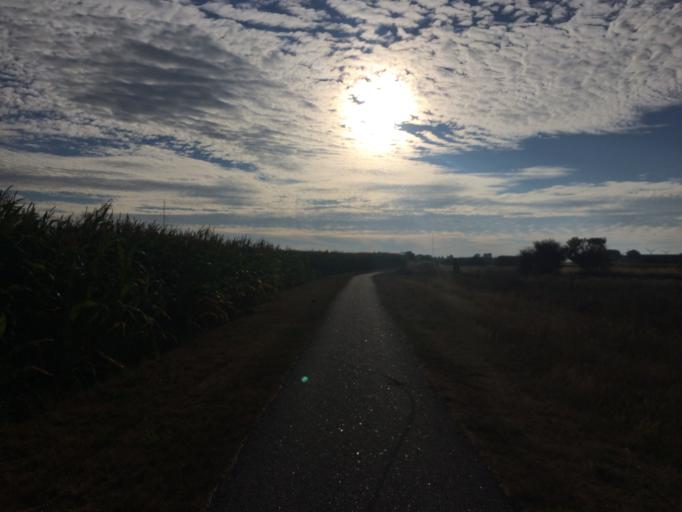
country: DK
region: Central Jutland
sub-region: Holstebro Kommune
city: Vinderup
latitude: 56.5998
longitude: 8.8588
